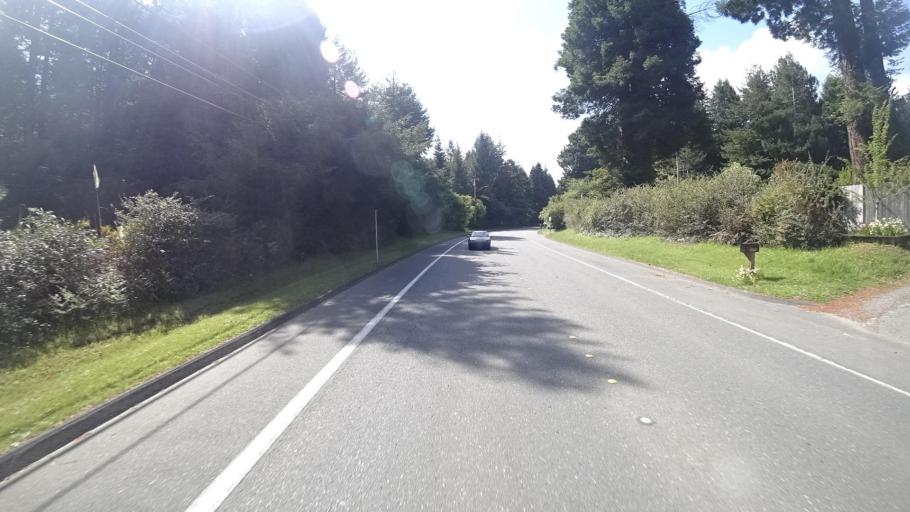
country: US
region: California
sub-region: Humboldt County
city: Cutten
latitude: 40.7527
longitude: -124.1455
